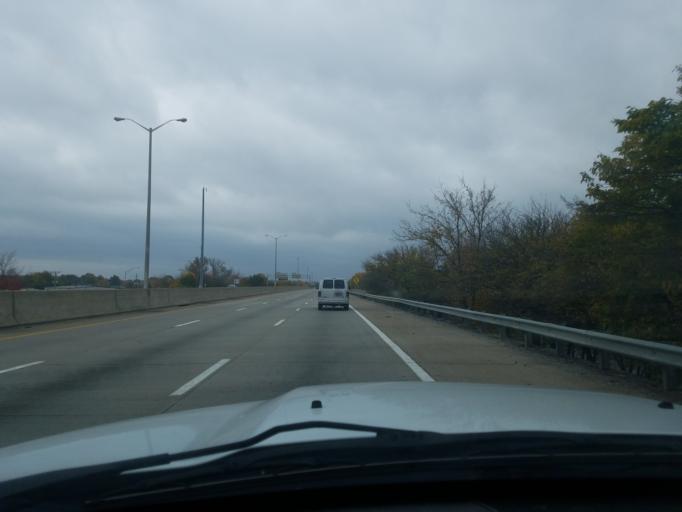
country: US
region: Kentucky
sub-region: Jefferson County
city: Shively
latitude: 38.2226
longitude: -85.8223
